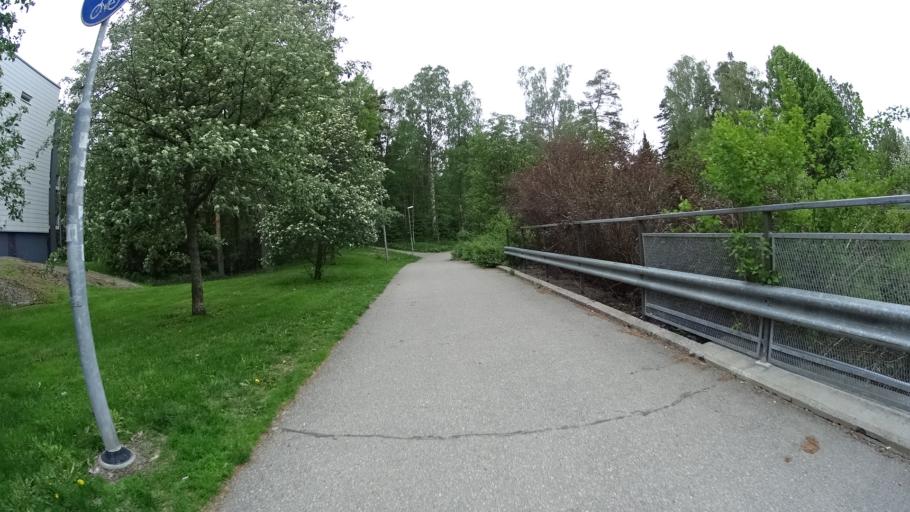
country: FI
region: Uusimaa
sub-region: Helsinki
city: Vantaa
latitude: 60.2422
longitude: 25.0748
